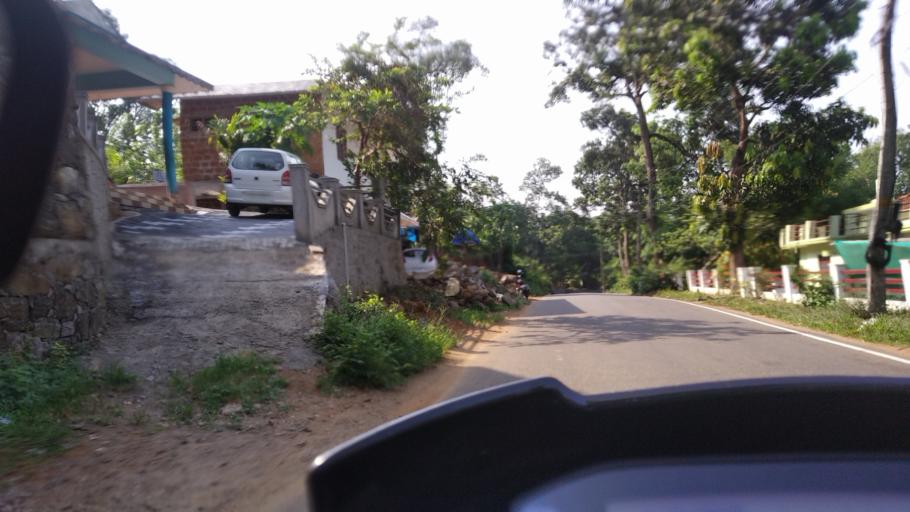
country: IN
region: Kerala
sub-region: Ernakulam
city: Piravam
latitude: 9.8225
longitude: 76.5507
